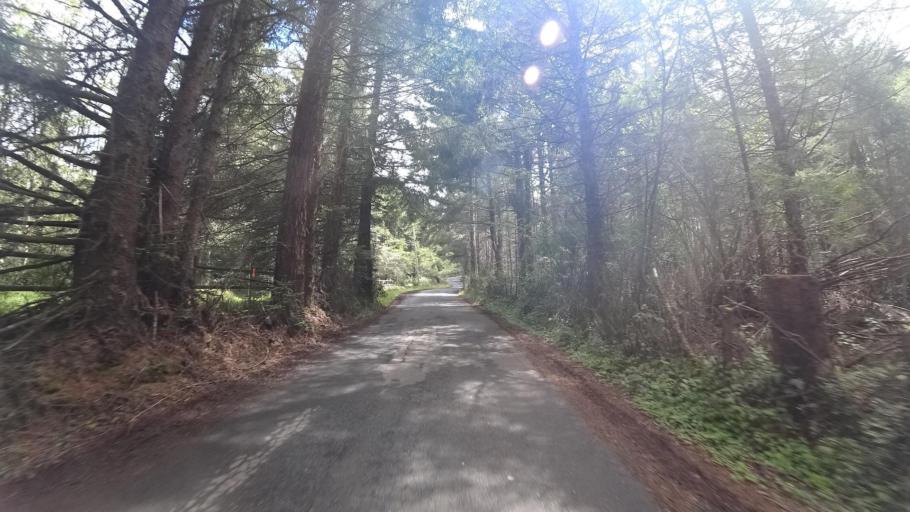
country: US
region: California
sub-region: Humboldt County
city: Bayside
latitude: 40.8343
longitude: -124.0194
